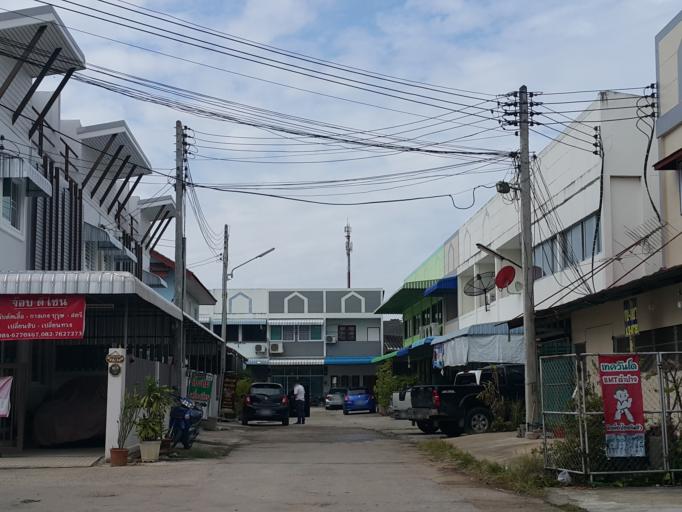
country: TH
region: Lampang
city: Lampang
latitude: 18.2996
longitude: 99.4980
